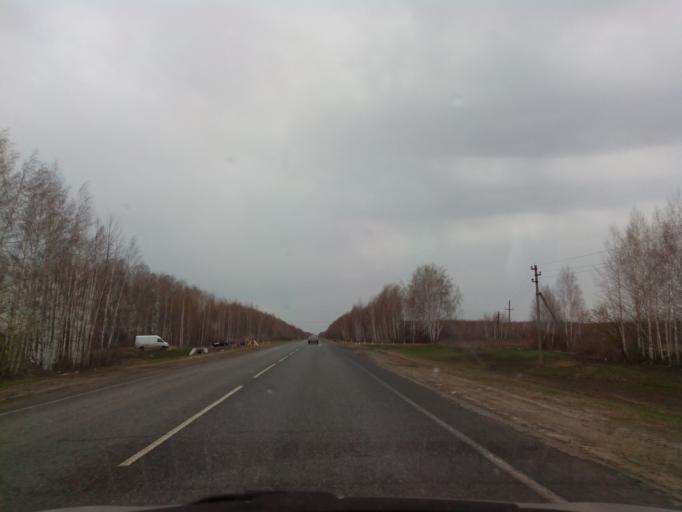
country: RU
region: Tambov
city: Michurinsk
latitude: 53.0481
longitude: 40.4742
